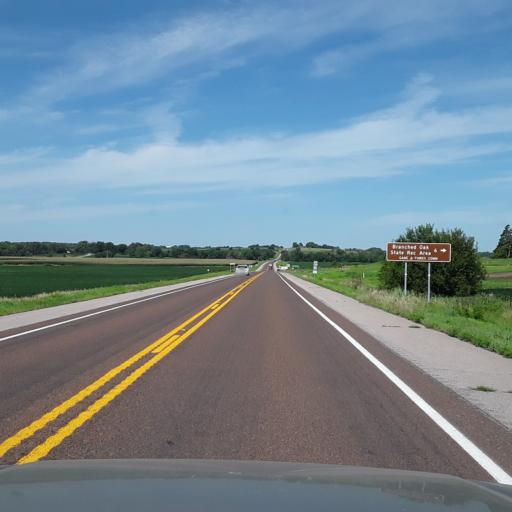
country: US
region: Nebraska
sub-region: Lancaster County
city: Lincoln
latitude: 40.8865
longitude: -96.8234
